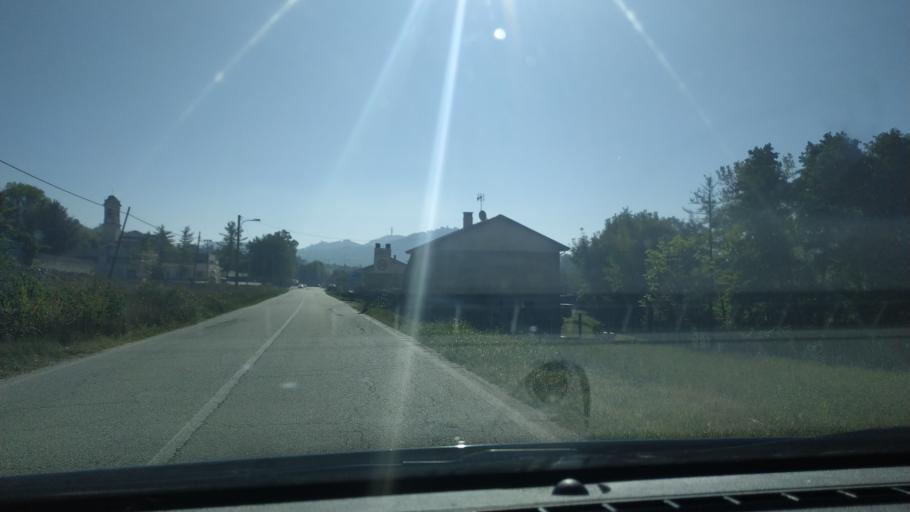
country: IT
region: Piedmont
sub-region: Provincia di Alessandria
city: Murisengo
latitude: 45.0887
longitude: 8.1456
